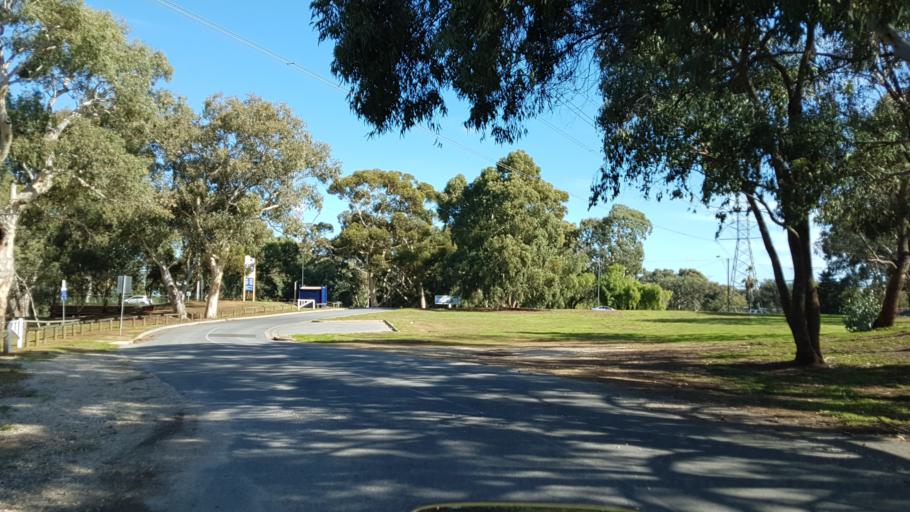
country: AU
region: South Australia
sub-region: Salisbury
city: Salisbury
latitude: -34.7575
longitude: 138.6355
